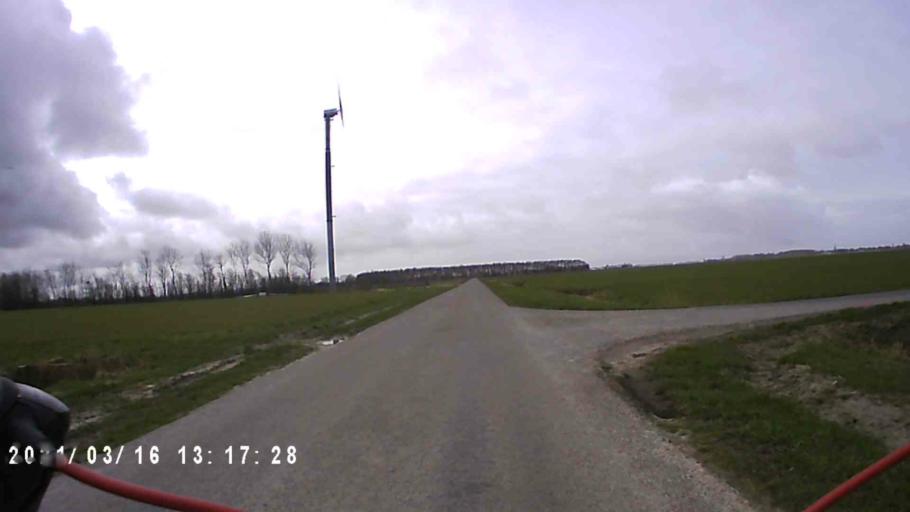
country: NL
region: Friesland
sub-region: Gemeente Het Bildt
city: Minnertsga
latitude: 53.2359
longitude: 5.5901
